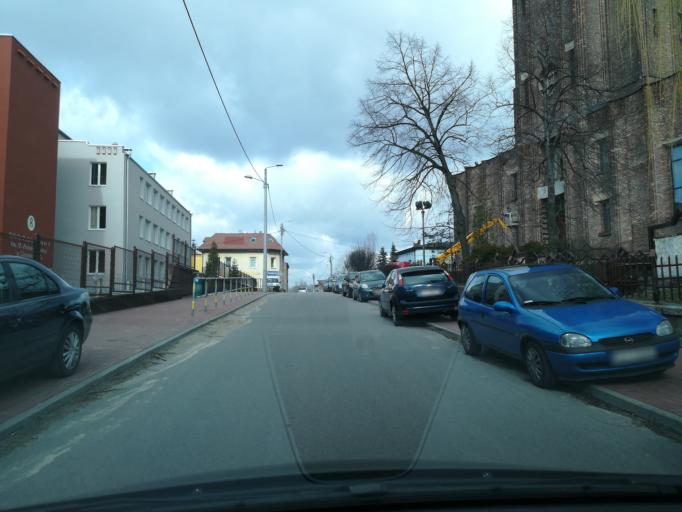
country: PL
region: Silesian Voivodeship
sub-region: Czestochowa
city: Czestochowa
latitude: 50.7920
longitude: 19.1333
